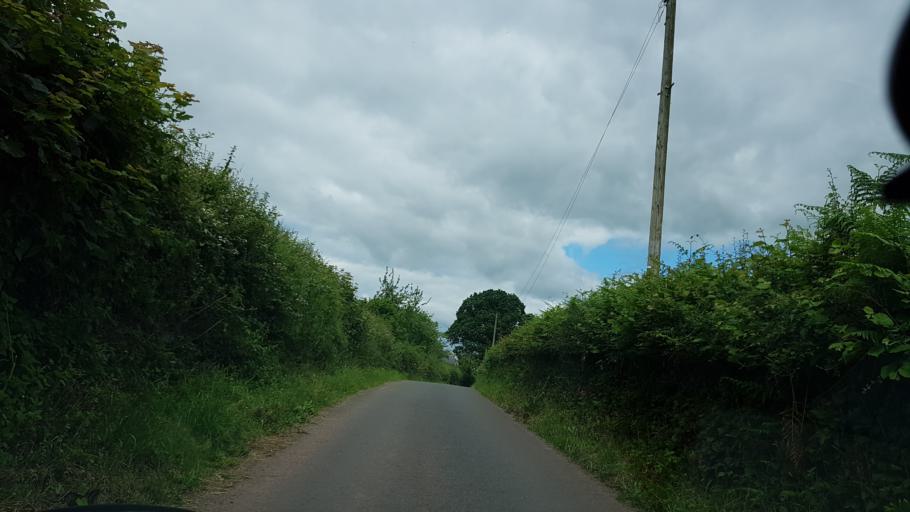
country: GB
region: Wales
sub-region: Monmouthshire
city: Llanarth
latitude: 51.8073
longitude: -2.8431
